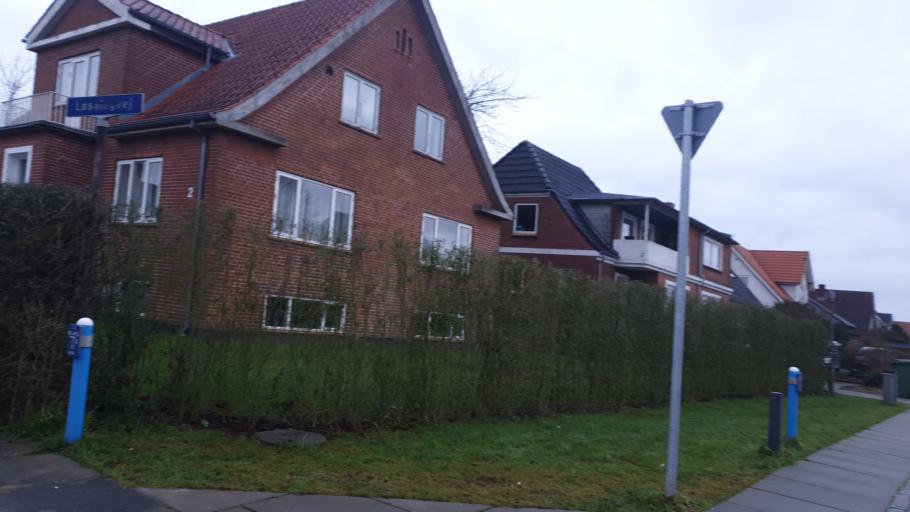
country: DK
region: Central Jutland
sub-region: Hedensted Kommune
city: Hedensted
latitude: 55.7716
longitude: 9.7038
